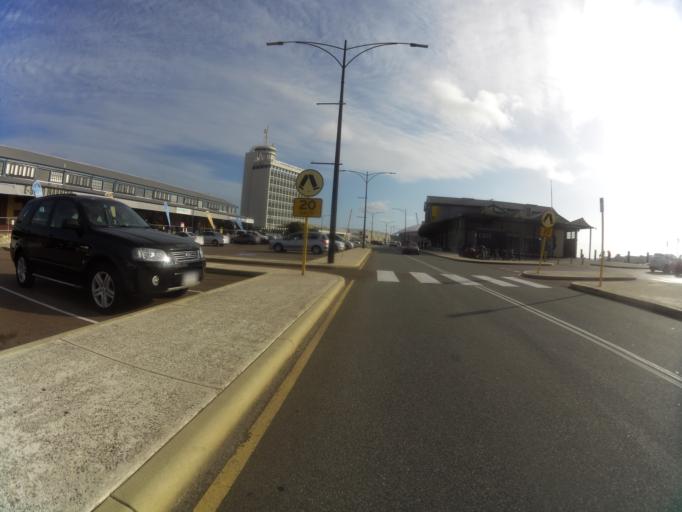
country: AU
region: Western Australia
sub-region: Fremantle
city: South Fremantle
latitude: -32.0530
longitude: 115.7423
